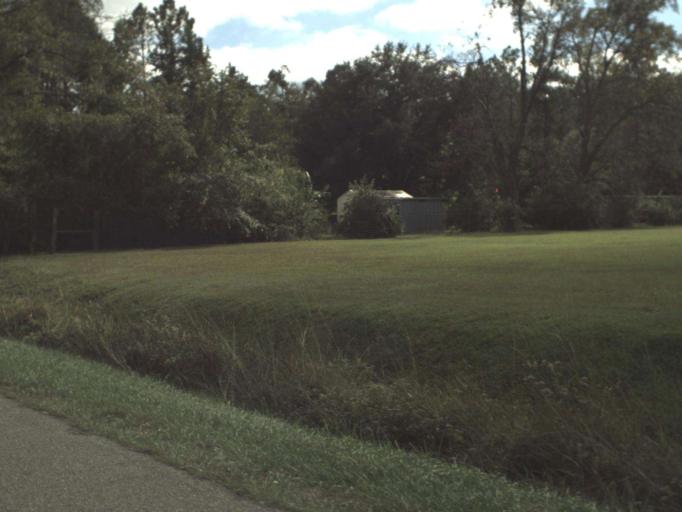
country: US
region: Florida
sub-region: Calhoun County
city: Blountstown
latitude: 30.5064
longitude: -85.1189
